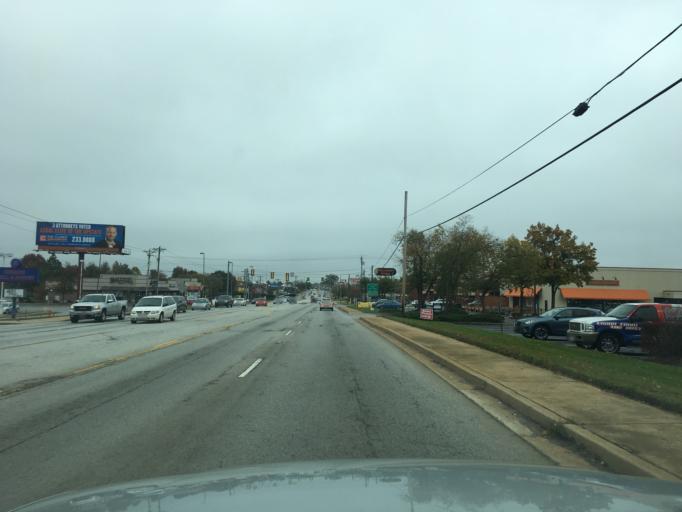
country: US
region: South Carolina
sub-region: Greenville County
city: Mauldin
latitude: 34.8219
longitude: -82.2861
